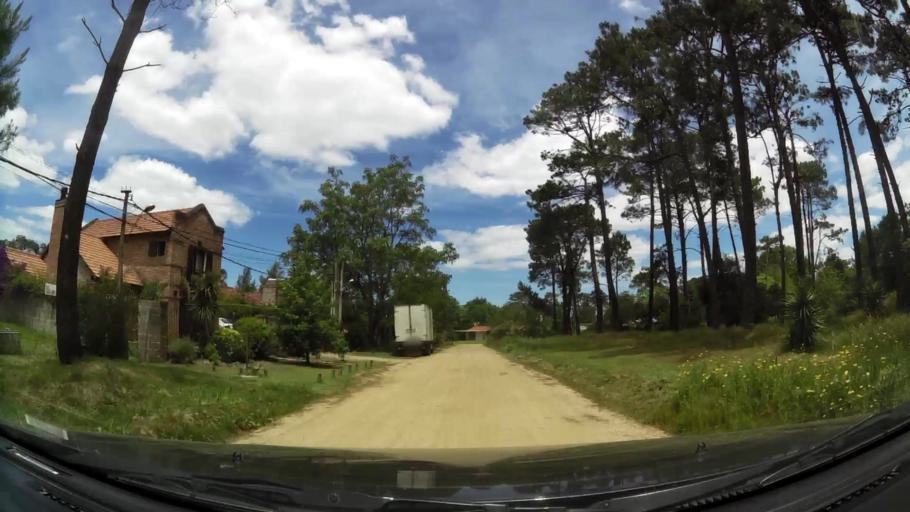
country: UY
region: Canelones
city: Pando
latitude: -34.7969
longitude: -55.8967
